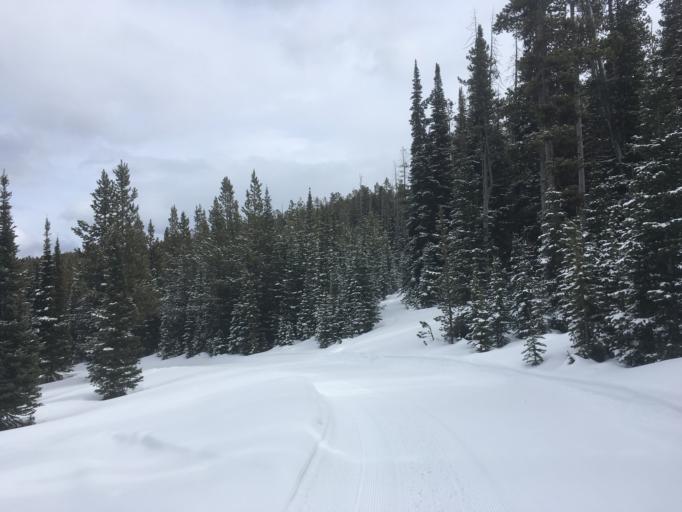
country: US
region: Montana
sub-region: Meagher County
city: White Sulphur Springs
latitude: 46.8437
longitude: -110.7064
